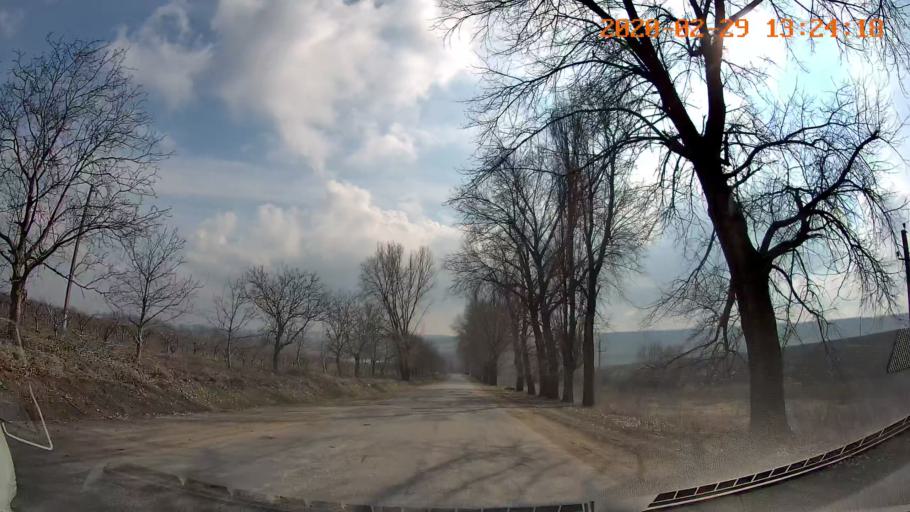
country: MD
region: Telenesti
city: Camenca
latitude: 47.9402
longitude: 28.6268
